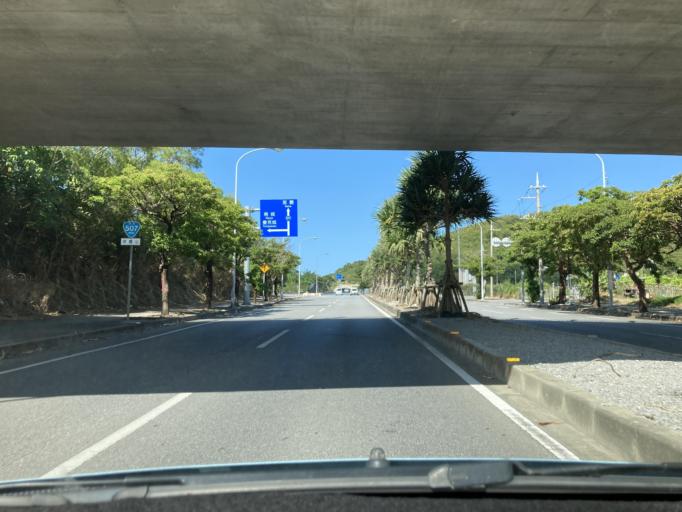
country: JP
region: Okinawa
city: Tomigusuku
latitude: 26.1836
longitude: 127.7224
